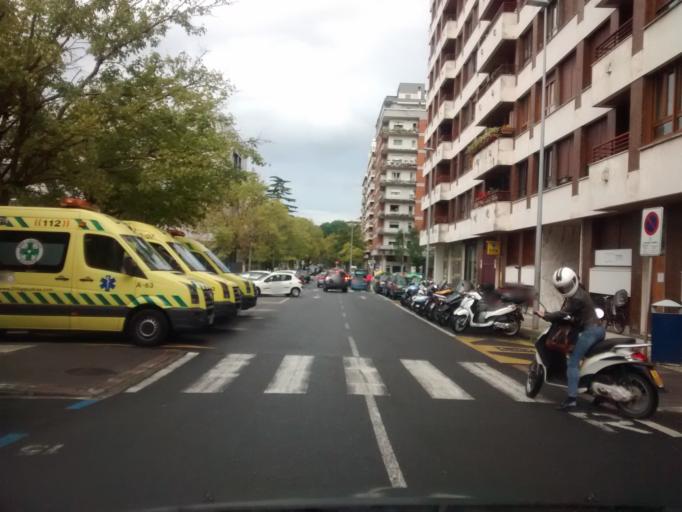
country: ES
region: Basque Country
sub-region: Provincia de Guipuzcoa
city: San Sebastian
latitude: 43.3057
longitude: -1.9821
